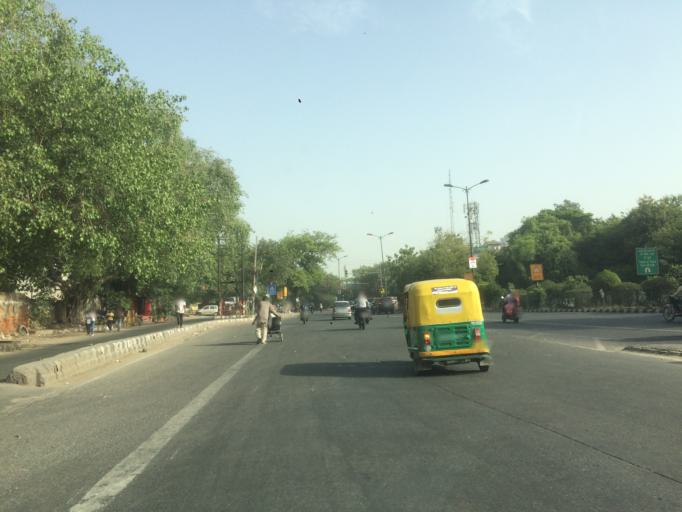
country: IN
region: Uttar Pradesh
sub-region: Gautam Buddha Nagar
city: Noida
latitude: 28.5596
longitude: 77.2676
